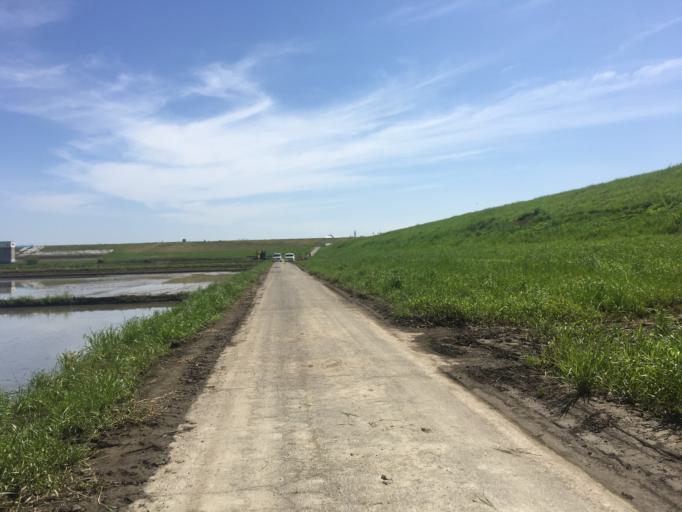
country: JP
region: Saitama
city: Shiki
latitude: 35.8770
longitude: 139.5804
